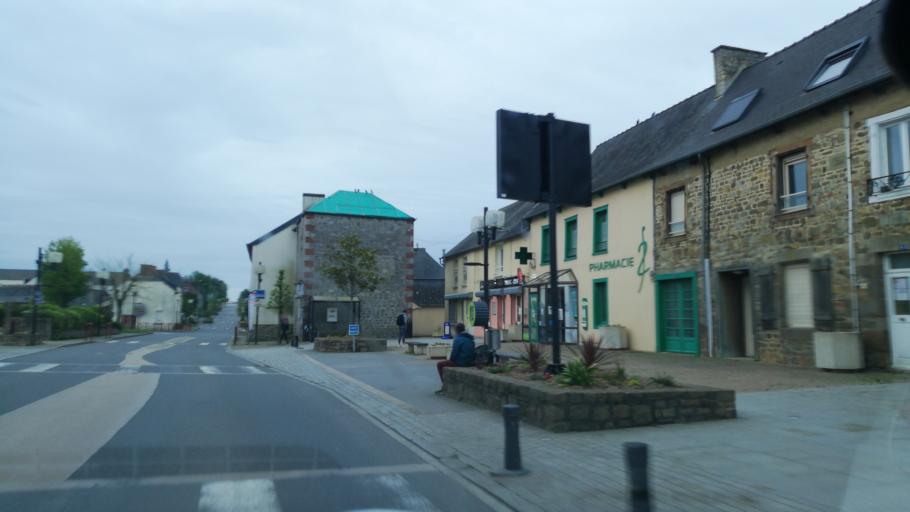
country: FR
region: Brittany
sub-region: Departement d'Ille-et-Vilaine
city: Irodouer
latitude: 48.2498
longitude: -1.9501
